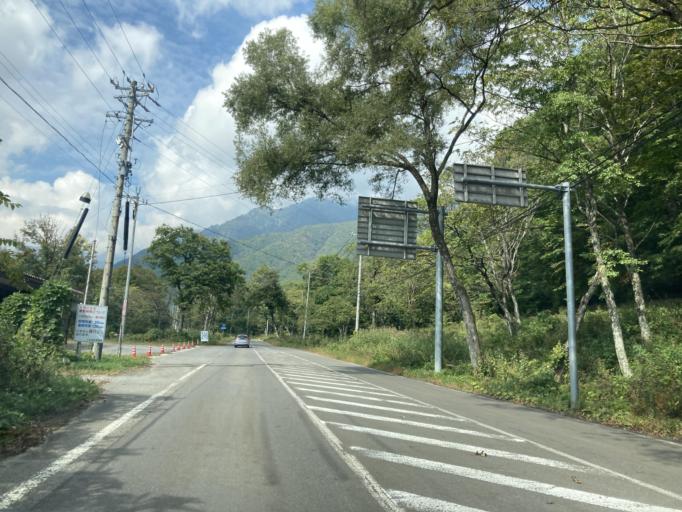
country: JP
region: Nagano
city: Omachi
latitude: 36.5355
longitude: 137.7899
